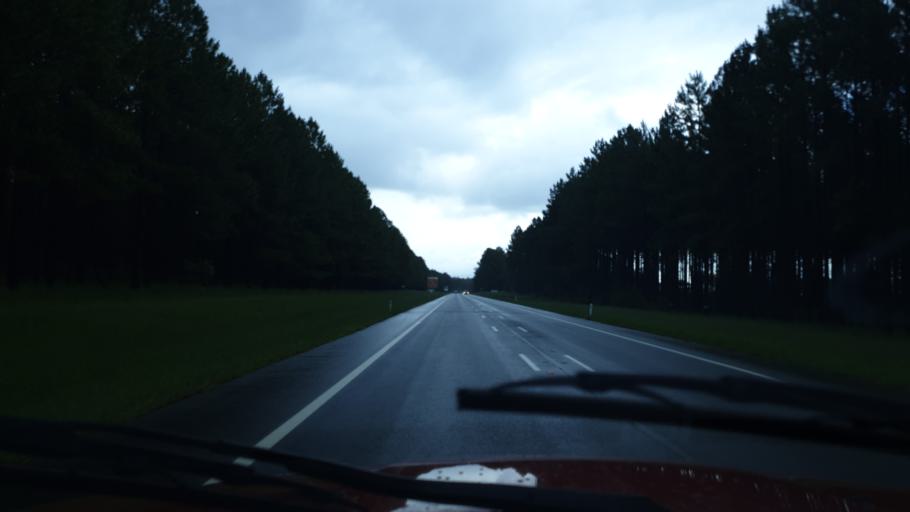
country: AU
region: Queensland
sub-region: Moreton Bay
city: Caboolture
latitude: -26.9810
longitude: 152.9689
